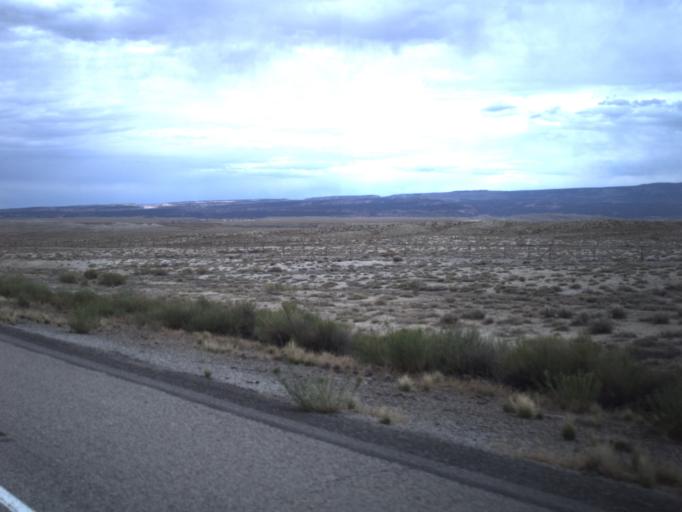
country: US
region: Utah
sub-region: Grand County
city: Moab
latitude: 38.9607
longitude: -109.3787
